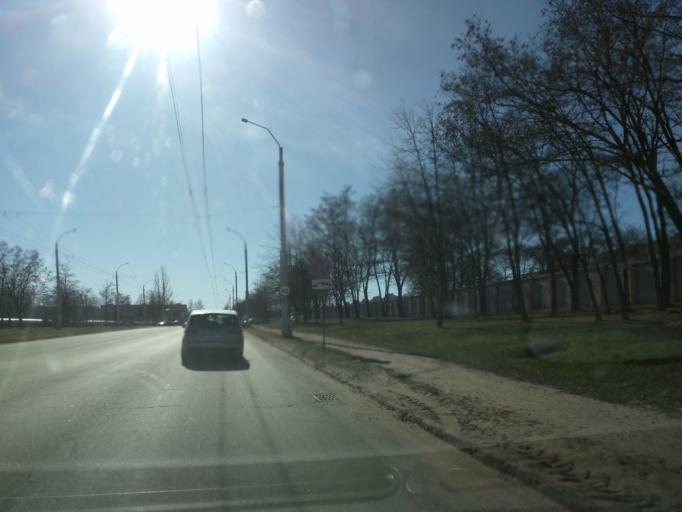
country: BY
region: Mogilev
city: Babruysk
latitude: 53.1812
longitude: 29.2070
